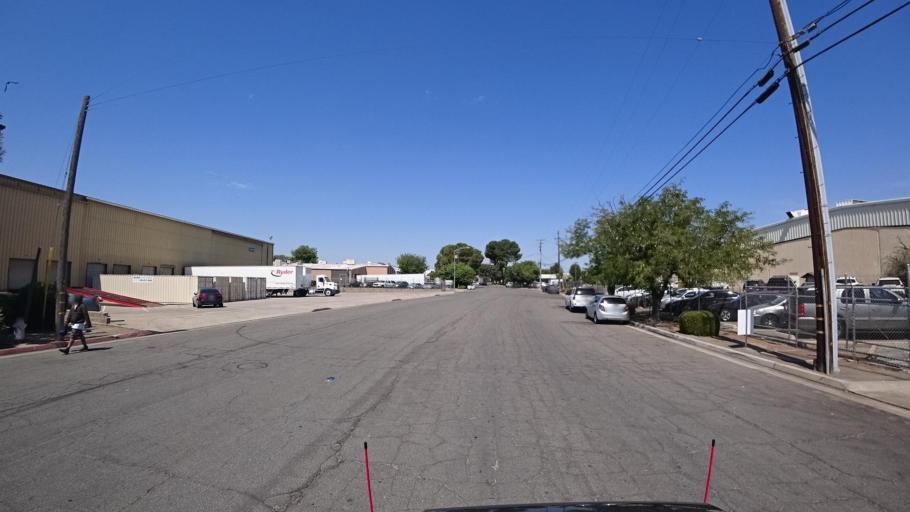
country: US
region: California
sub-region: Fresno County
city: Tarpey Village
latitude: 36.7813
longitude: -119.6957
